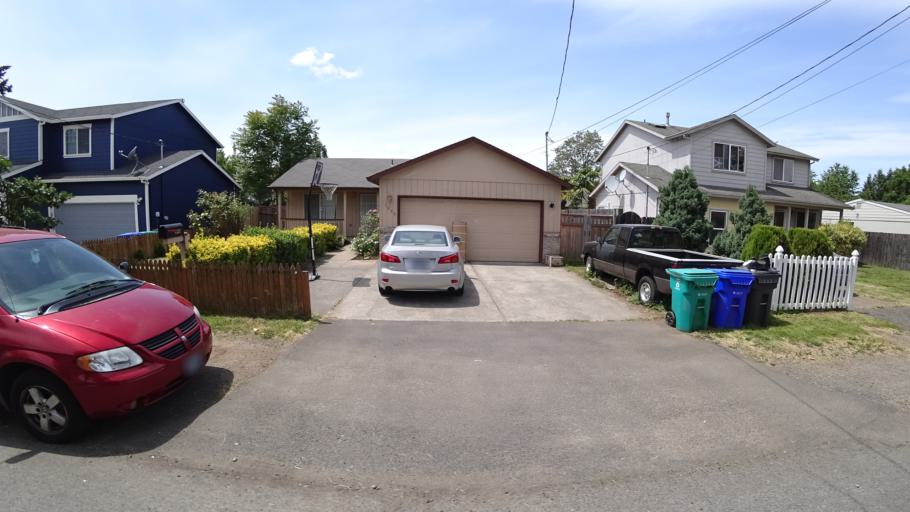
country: US
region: Oregon
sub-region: Multnomah County
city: Lents
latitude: 45.4662
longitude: -122.5969
